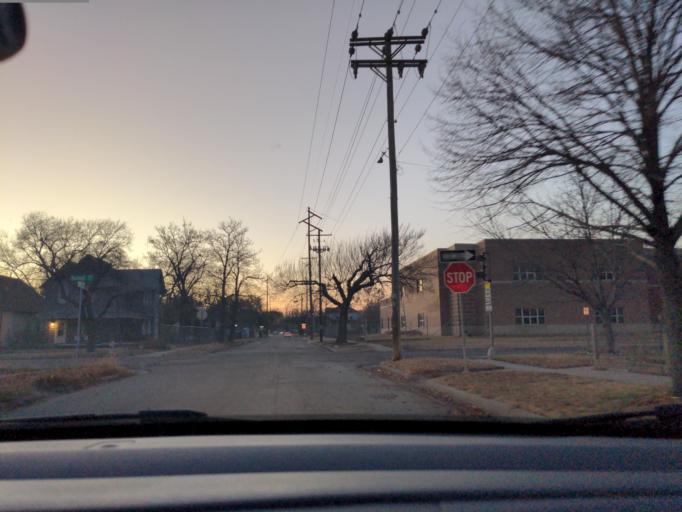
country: US
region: Kansas
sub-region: Sedgwick County
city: Wichita
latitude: 37.7045
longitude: -97.3365
